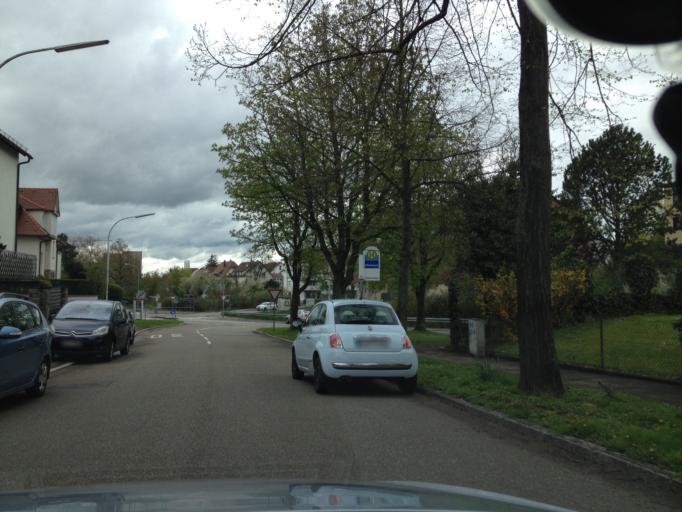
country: DE
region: Baden-Wuerttemberg
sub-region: Regierungsbezirk Stuttgart
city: Heilbronn
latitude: 49.1310
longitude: 9.2319
